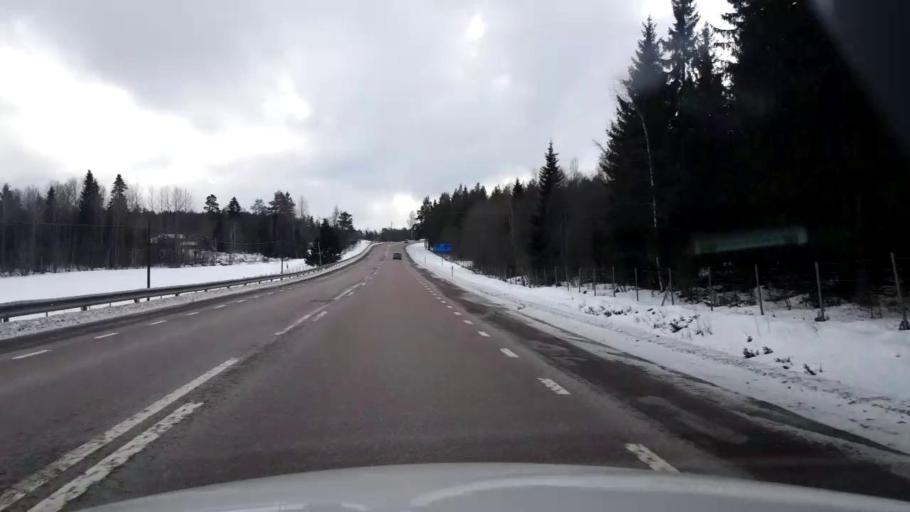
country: SE
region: Gaevleborg
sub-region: Nordanstigs Kommun
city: Bergsjoe
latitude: 61.9222
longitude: 17.2127
